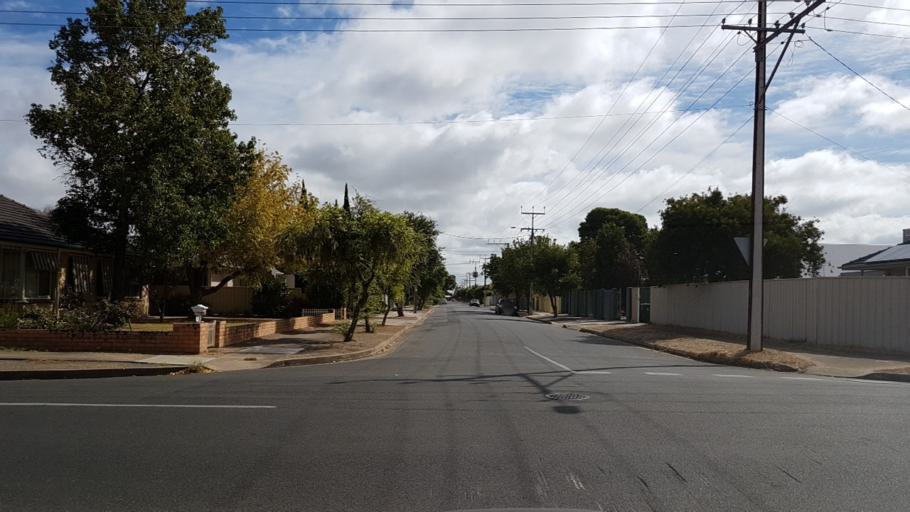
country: AU
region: South Australia
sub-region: Marion
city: Plympton Park
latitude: -34.9885
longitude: 138.5502
